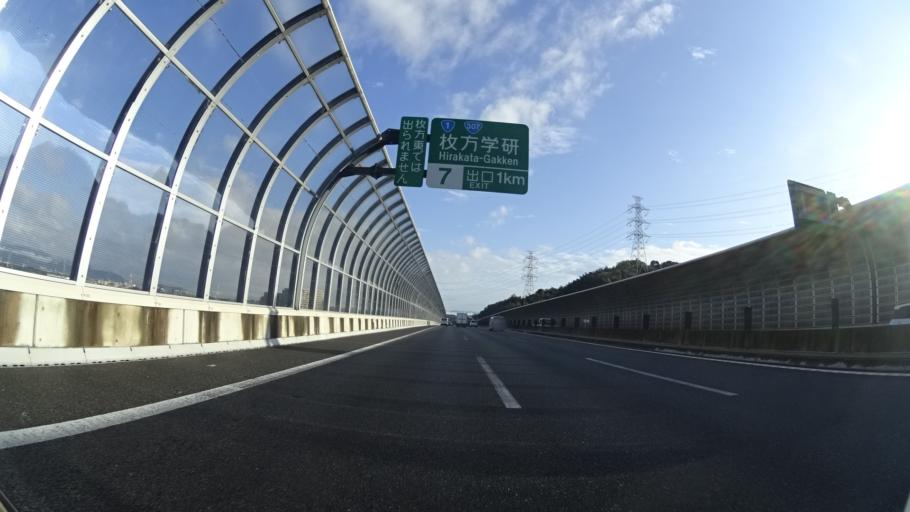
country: JP
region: Osaka
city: Hirakata
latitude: 34.7992
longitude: 135.7040
